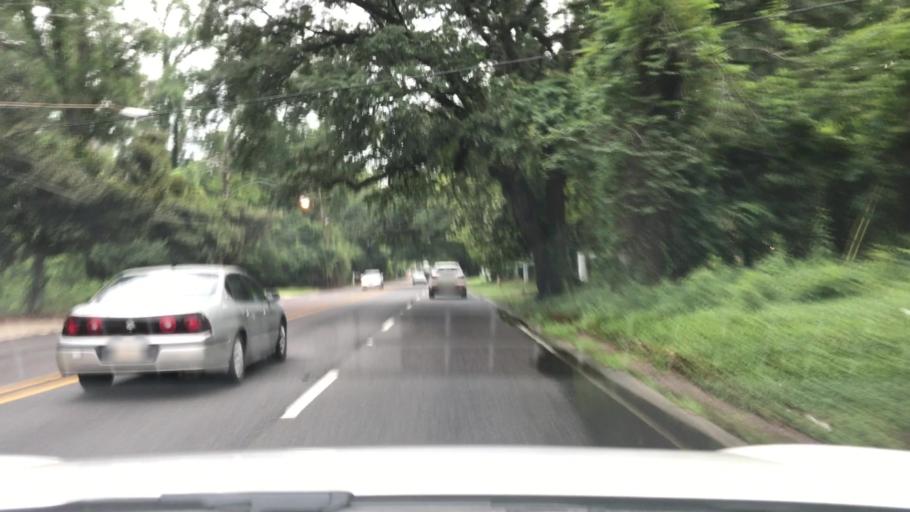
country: US
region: Louisiana
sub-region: East Baton Rouge Parish
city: Baton Rouge
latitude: 30.4556
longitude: -91.1392
